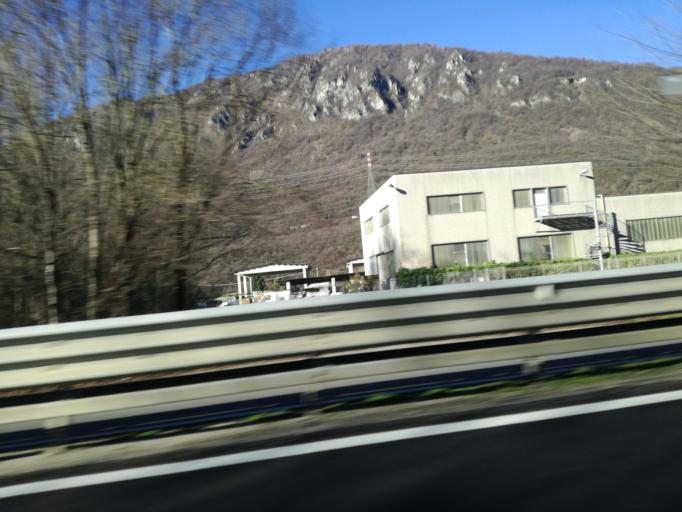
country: IT
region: Lombardy
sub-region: Provincia di Bergamo
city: Sovere
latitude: 45.8027
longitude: 10.0211
